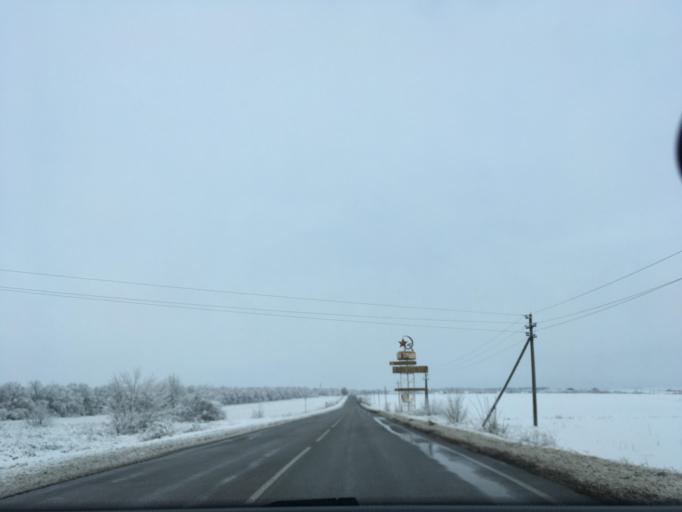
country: RU
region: Voronezj
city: Ol'khovatka
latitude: 50.0239
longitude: 39.0647
